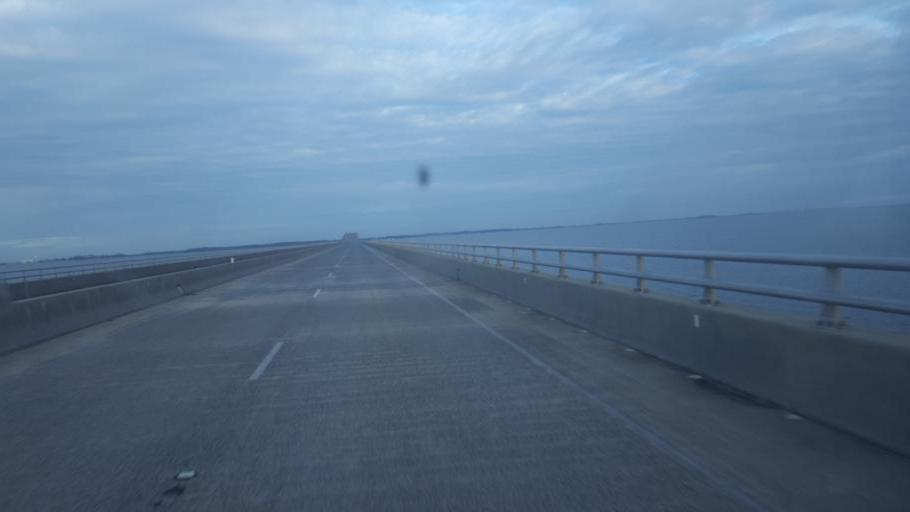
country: US
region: North Carolina
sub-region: Dare County
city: Manteo
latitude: 35.8839
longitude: -75.7018
